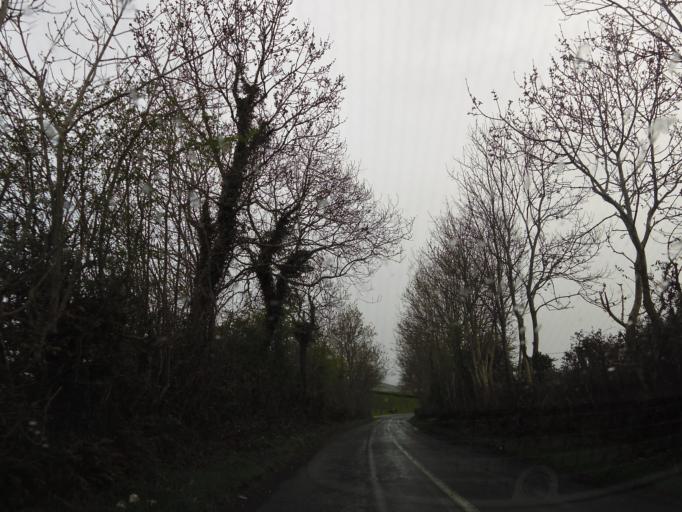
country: IE
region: Connaught
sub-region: Sligo
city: Collooney
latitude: 54.1729
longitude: -8.5085
